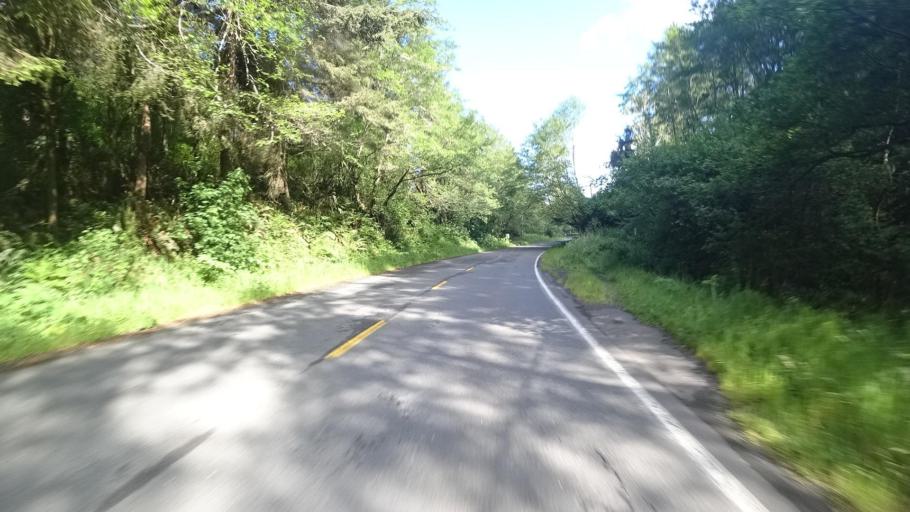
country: US
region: California
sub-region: Humboldt County
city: McKinleyville
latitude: 40.9915
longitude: -124.1115
